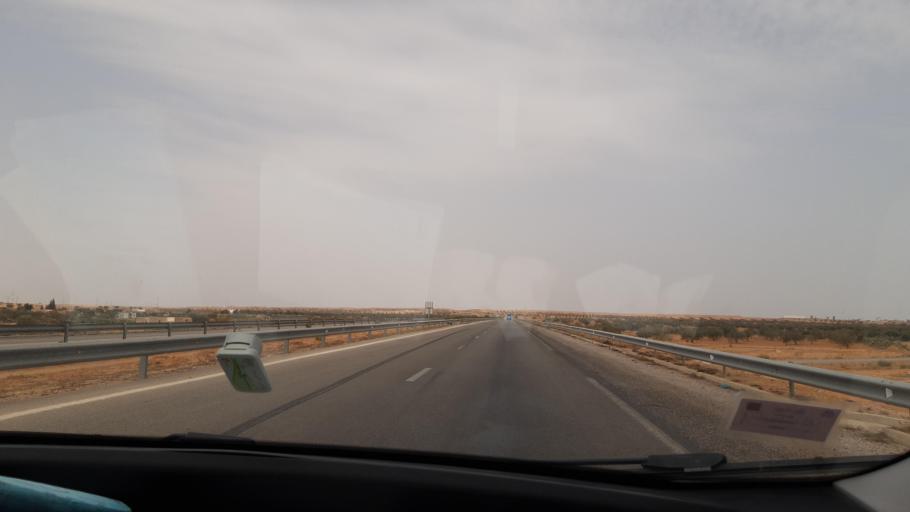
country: TN
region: Safaqis
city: Sfax
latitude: 34.7396
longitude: 10.5967
